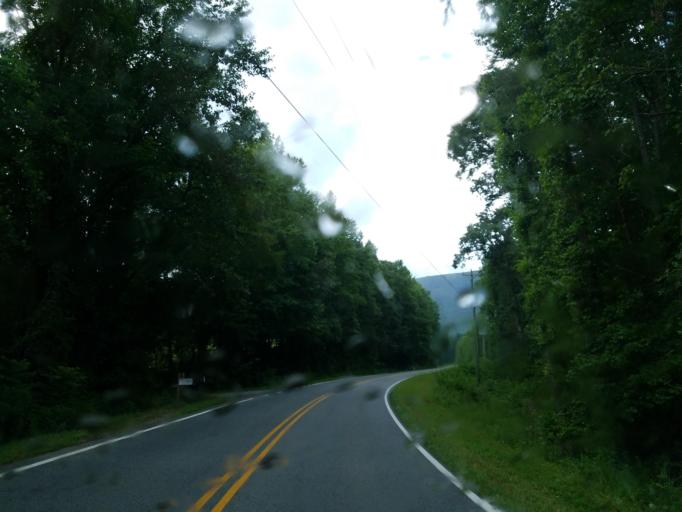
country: US
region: Georgia
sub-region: Gilmer County
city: Ellijay
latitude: 34.6741
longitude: -84.3834
